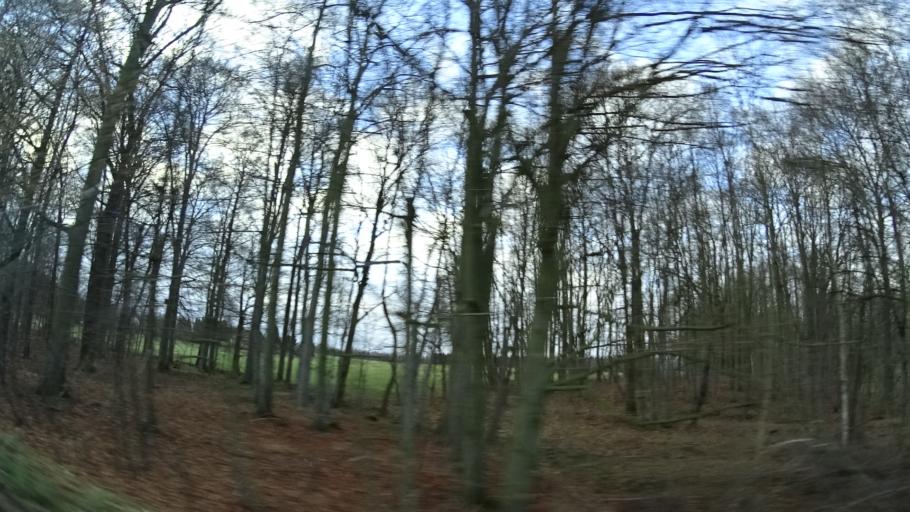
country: DE
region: Thuringia
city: Auma
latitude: 50.6782
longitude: 11.9225
